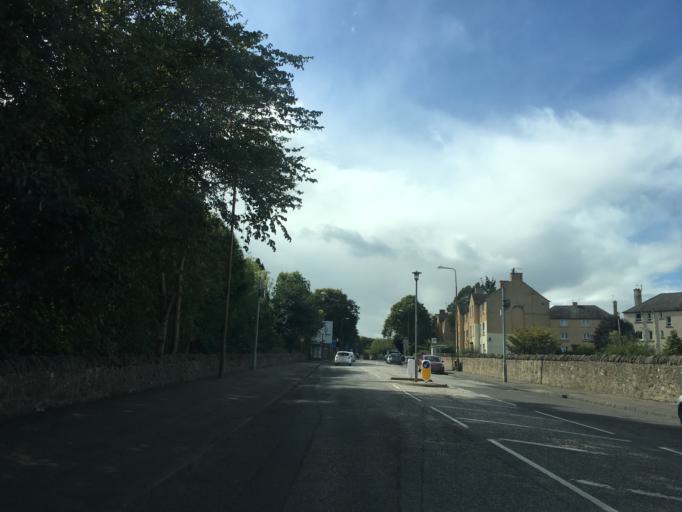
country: GB
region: Scotland
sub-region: West Lothian
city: Seafield
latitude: 55.9306
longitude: -3.1580
